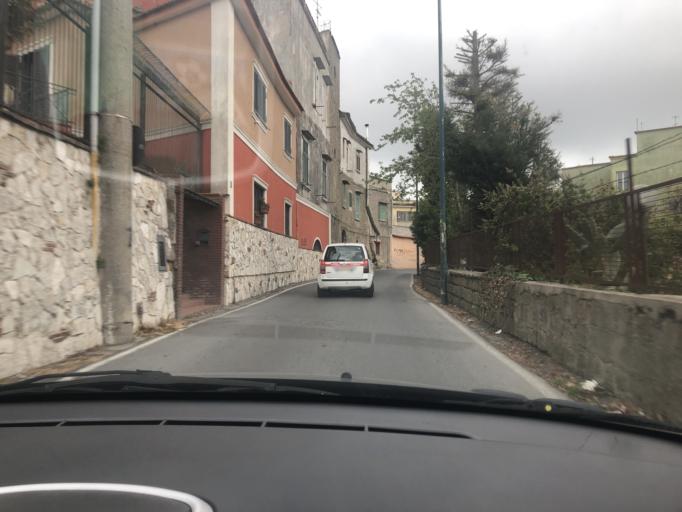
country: IT
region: Campania
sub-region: Provincia di Napoli
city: Torre Caracciolo
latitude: 40.8662
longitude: 14.1888
